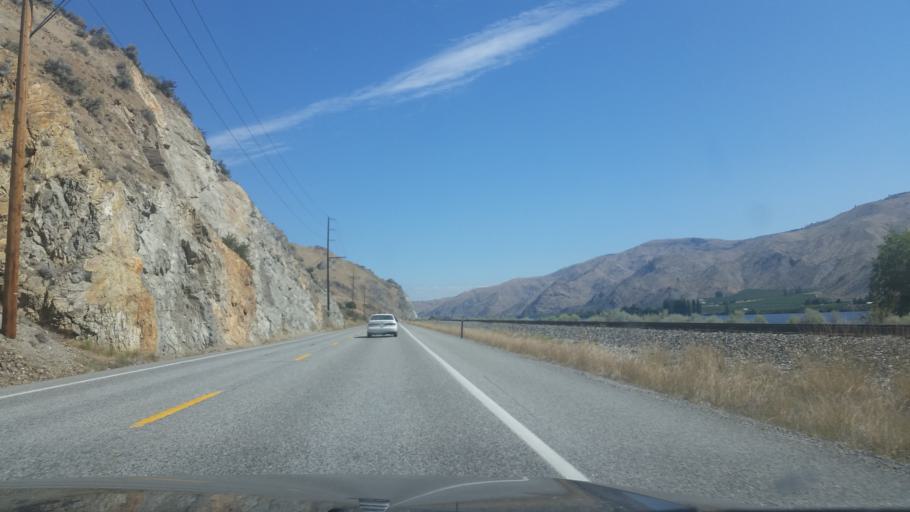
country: US
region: Washington
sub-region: Chelan County
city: Entiat
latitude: 47.6399
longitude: -120.2358
